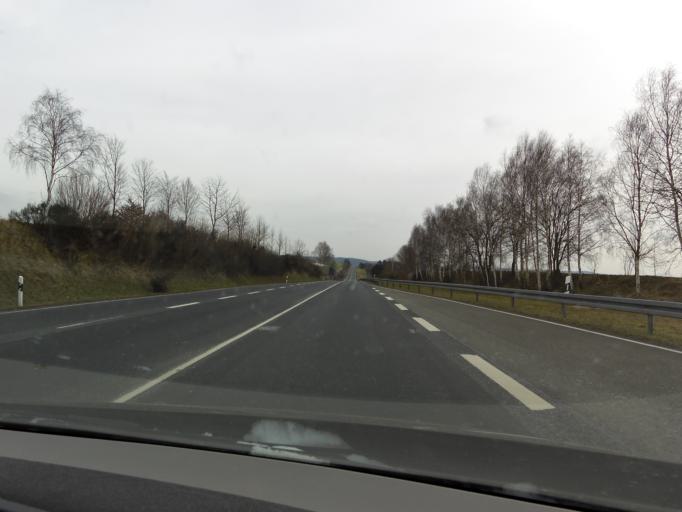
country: DE
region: Thuringia
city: Breitungen
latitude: 50.7689
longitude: 10.3326
